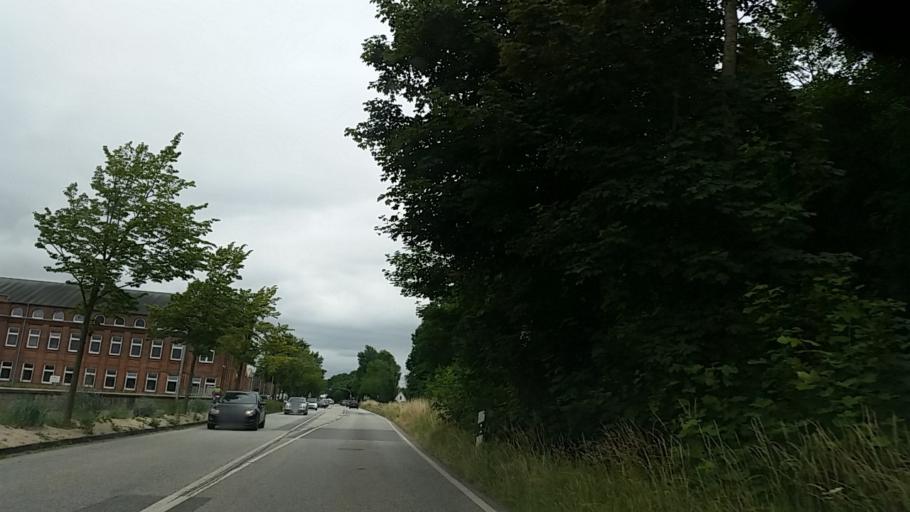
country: DE
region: Schleswig-Holstein
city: Eckernforde
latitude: 54.4549
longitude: 9.8489
